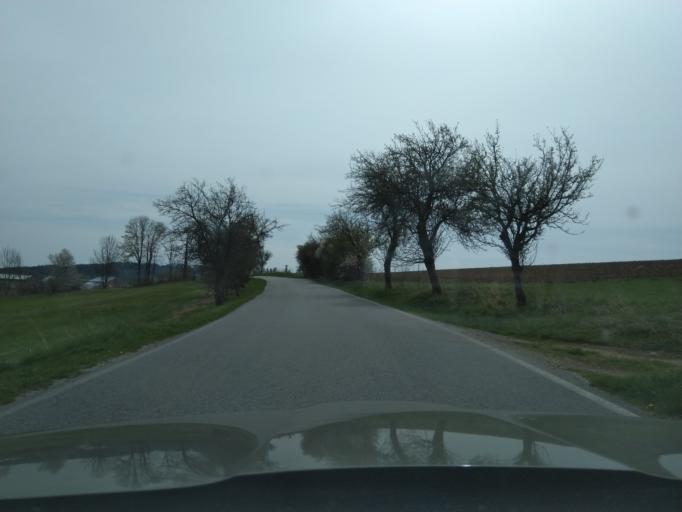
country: CZ
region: Jihocesky
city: Vacov
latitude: 49.1442
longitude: 13.7111
